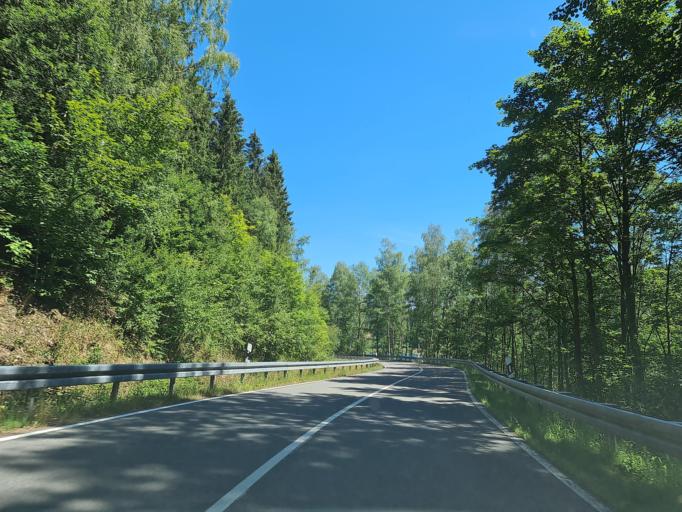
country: DE
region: Saxony
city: Rechenberg-Bienenmuhle
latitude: 50.7064
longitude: 13.5288
